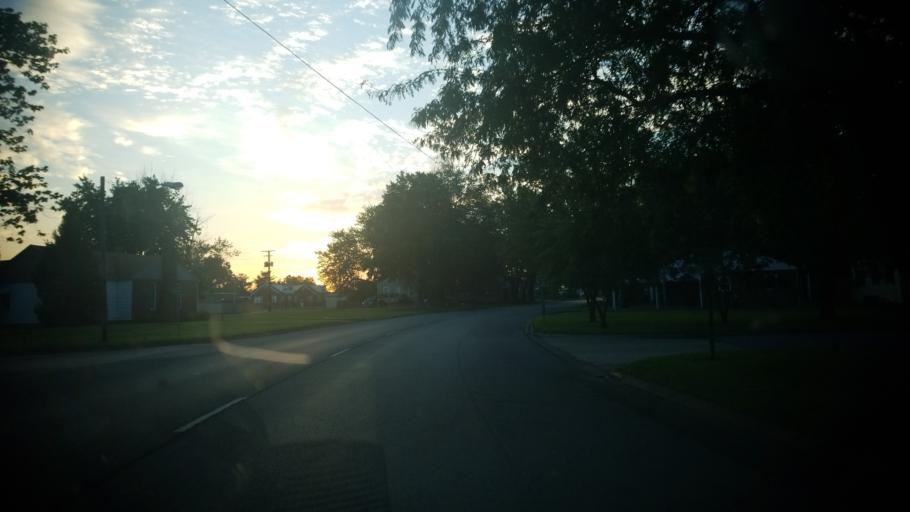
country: US
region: Illinois
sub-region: Wayne County
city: Fairfield
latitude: 38.3786
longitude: -88.3803
